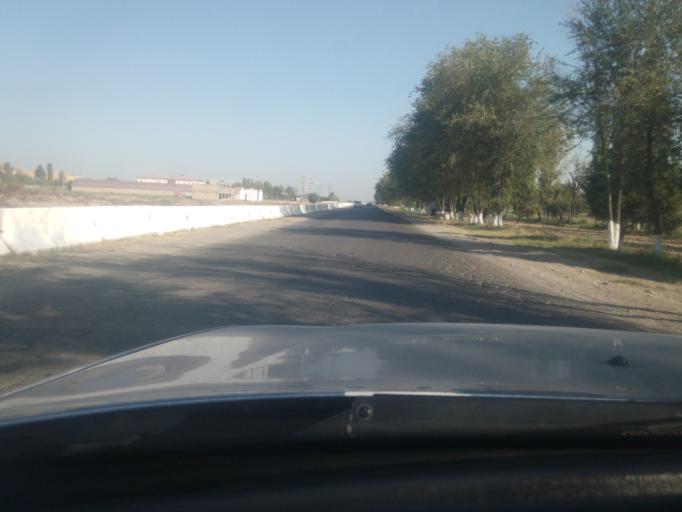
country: UZ
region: Sirdaryo
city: Guliston
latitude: 40.5130
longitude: 68.7946
